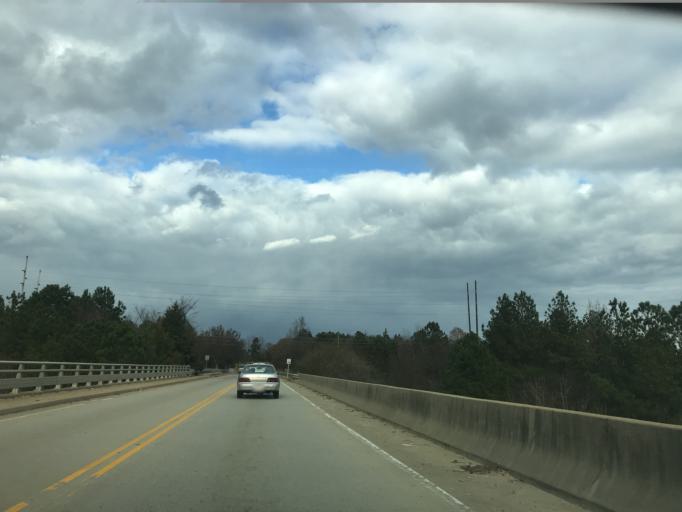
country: US
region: North Carolina
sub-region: Wake County
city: Raleigh
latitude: 35.7831
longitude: -78.5614
